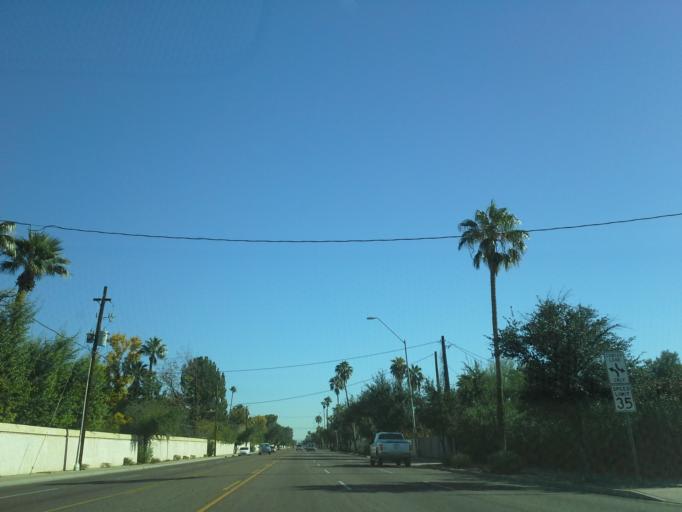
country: US
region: Arizona
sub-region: Maricopa County
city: Phoenix
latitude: 33.4802
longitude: -112.0637
